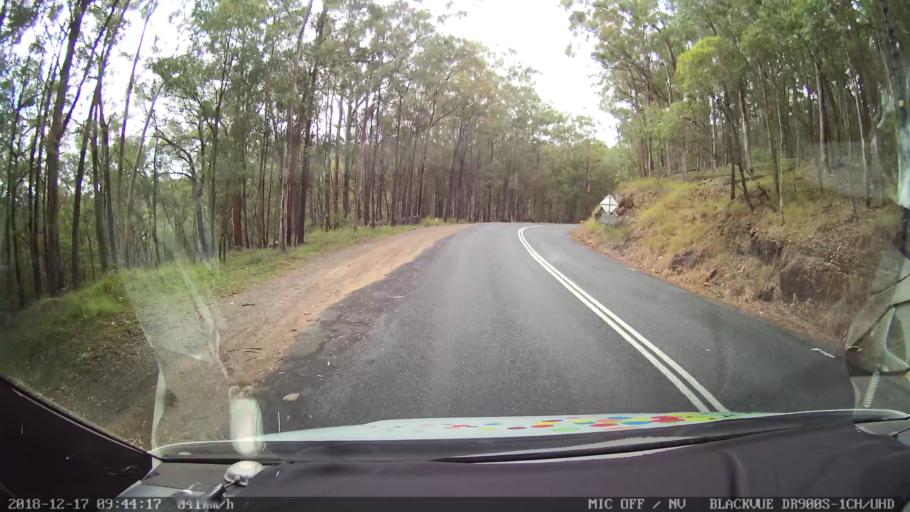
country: AU
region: New South Wales
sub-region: Tenterfield Municipality
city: Carrolls Creek
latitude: -28.9250
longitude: 152.3244
